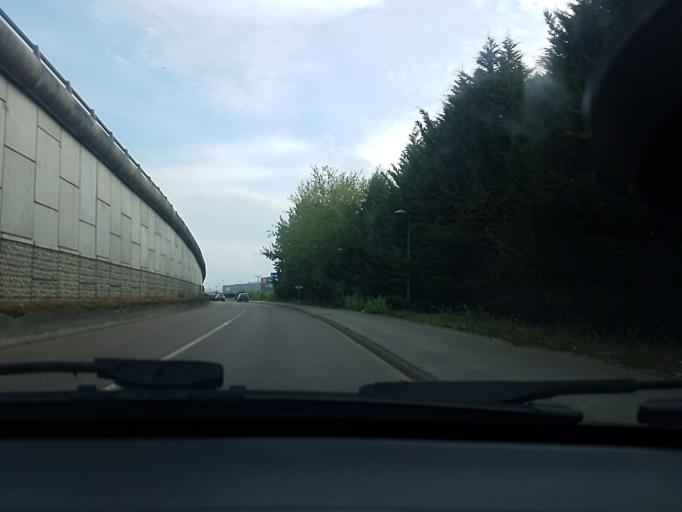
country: FR
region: Bourgogne
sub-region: Departement de Saone-et-Loire
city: Saint-Marcel
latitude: 46.7703
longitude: 4.8708
